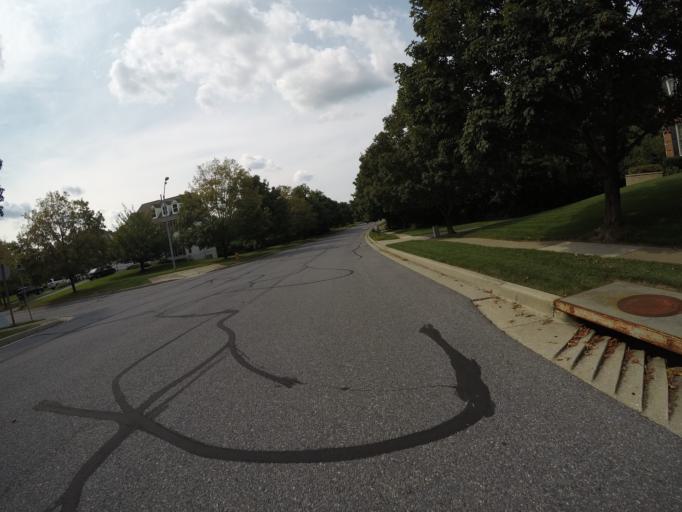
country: US
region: Maryland
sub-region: Howard County
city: Columbia
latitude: 39.3040
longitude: -76.8735
